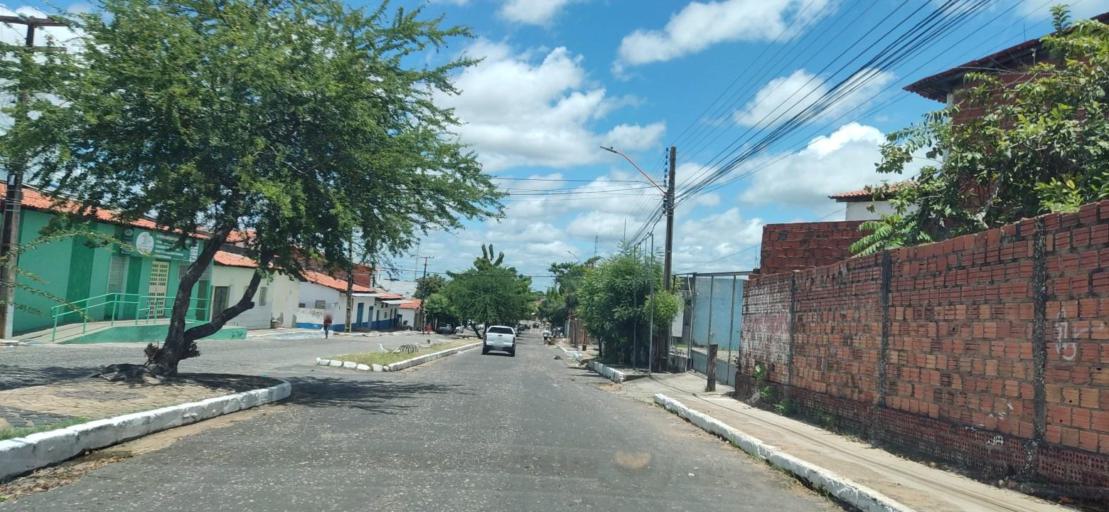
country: BR
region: Piaui
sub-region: Teresina
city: Teresina
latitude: -5.1463
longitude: -42.7819
